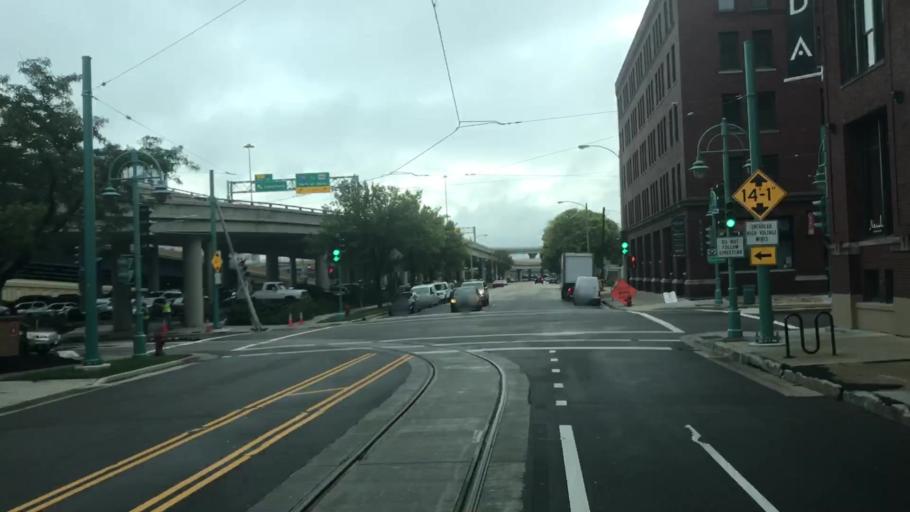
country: US
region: Wisconsin
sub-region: Milwaukee County
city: Milwaukee
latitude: 43.0350
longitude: -87.9066
